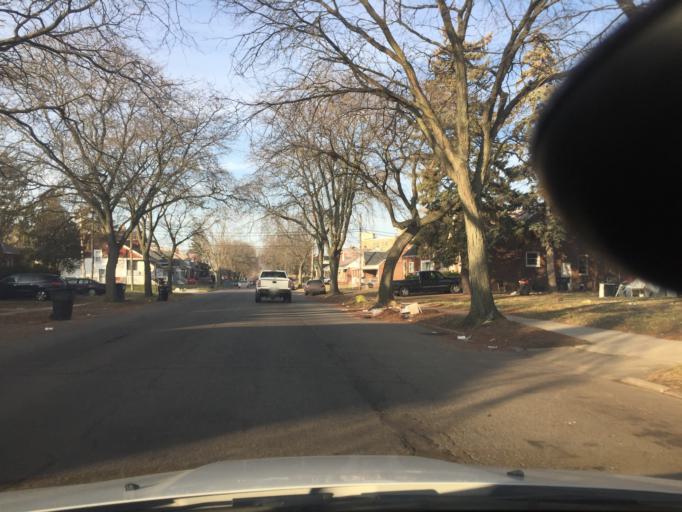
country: US
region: Michigan
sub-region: Macomb County
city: Eastpointe
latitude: 42.4427
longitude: -82.9679
